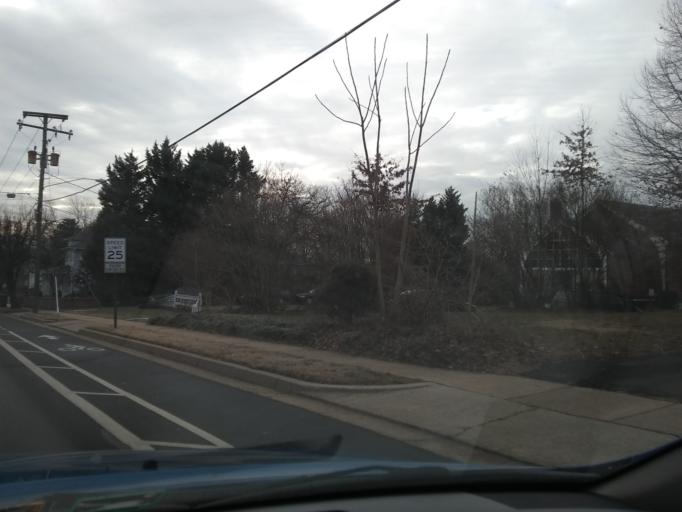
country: US
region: Virginia
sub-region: Fairfax County
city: Huntington
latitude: 38.8187
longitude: -77.0768
